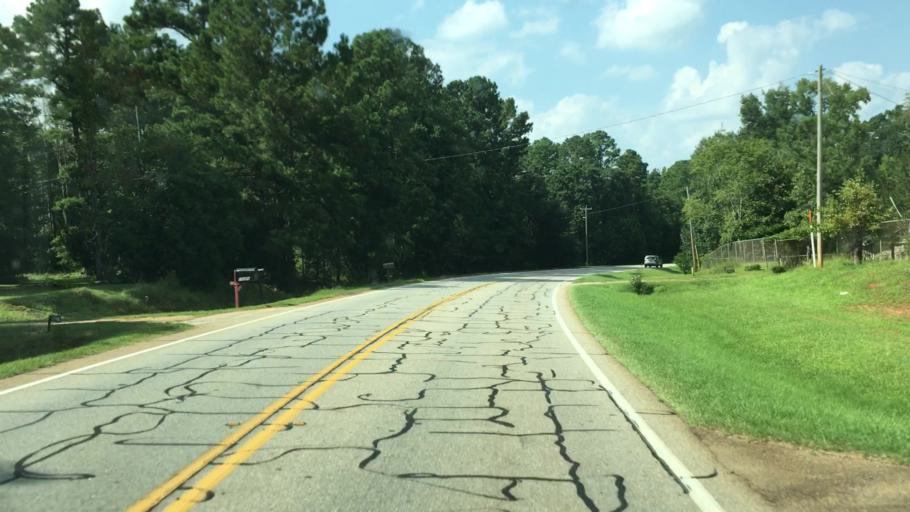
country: US
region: Georgia
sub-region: Jasper County
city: Monticello
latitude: 33.2671
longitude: -83.7195
